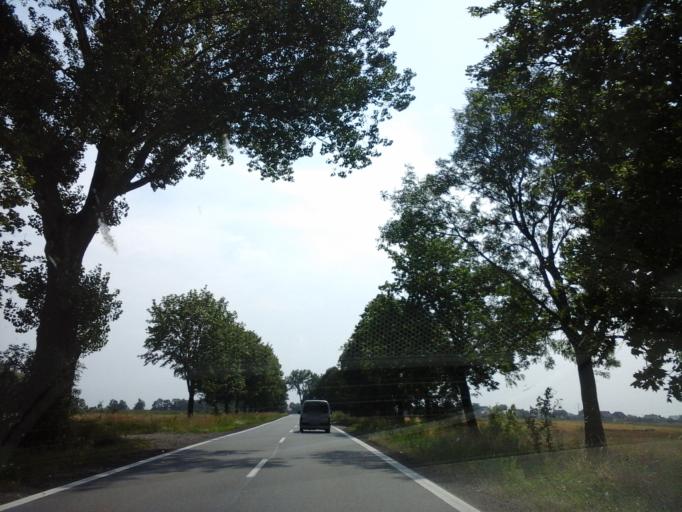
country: PL
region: Lower Silesian Voivodeship
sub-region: Powiat wroclawski
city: Zerniki Wroclawskie
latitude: 51.0034
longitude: 17.0650
